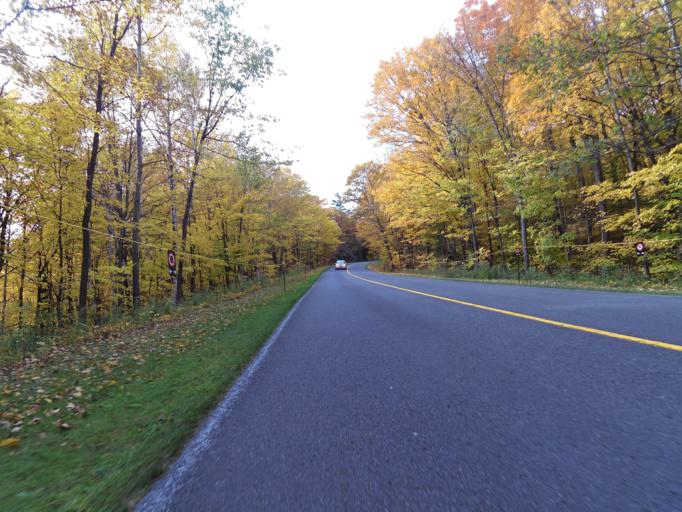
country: CA
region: Quebec
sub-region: Outaouais
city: Gatineau
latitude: 45.4816
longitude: -75.8543
